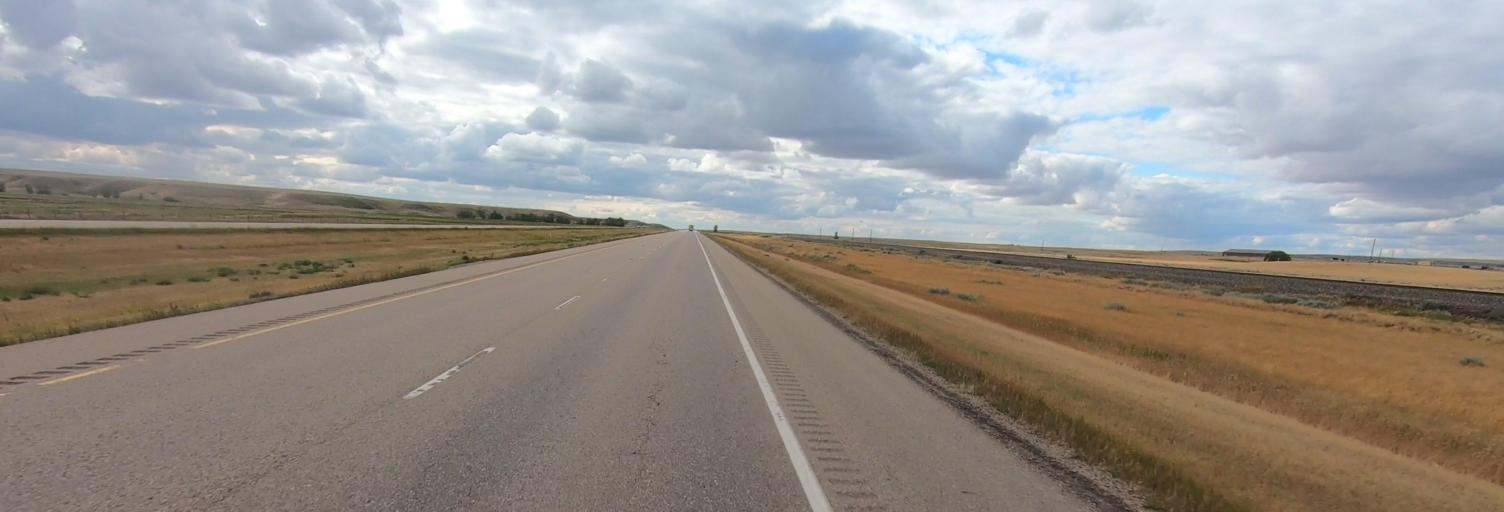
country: CA
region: Alberta
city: Medicine Hat
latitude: 49.9411
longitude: -110.1812
